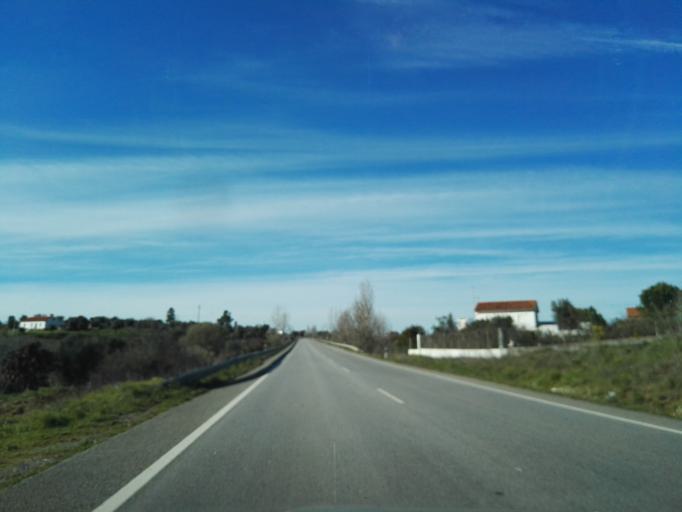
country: PT
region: Santarem
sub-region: Abrantes
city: Alferrarede
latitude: 39.4791
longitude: -8.0854
